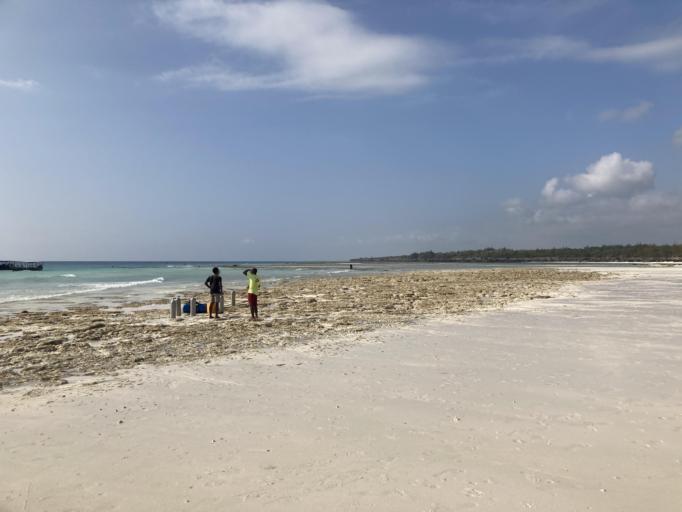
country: TZ
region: Zanzibar North
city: Kijini
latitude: -5.8085
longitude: 39.3606
